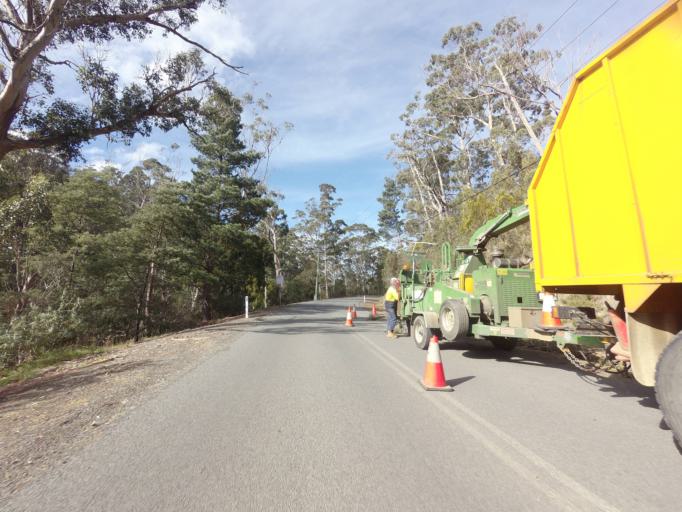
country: AU
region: Tasmania
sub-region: Clarence
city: Sandford
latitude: -43.1137
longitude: 147.7512
